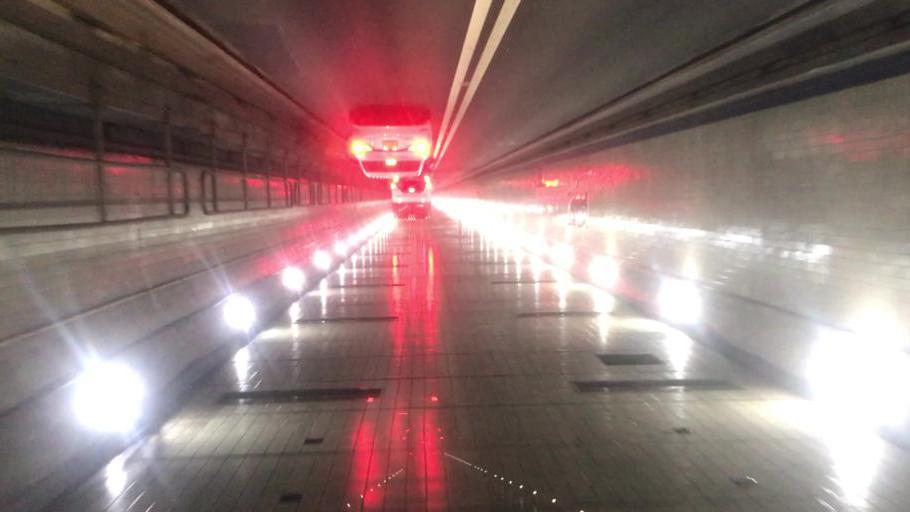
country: US
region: New Jersey
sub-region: Hudson County
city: Weehawken
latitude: 40.7575
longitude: -74.0031
